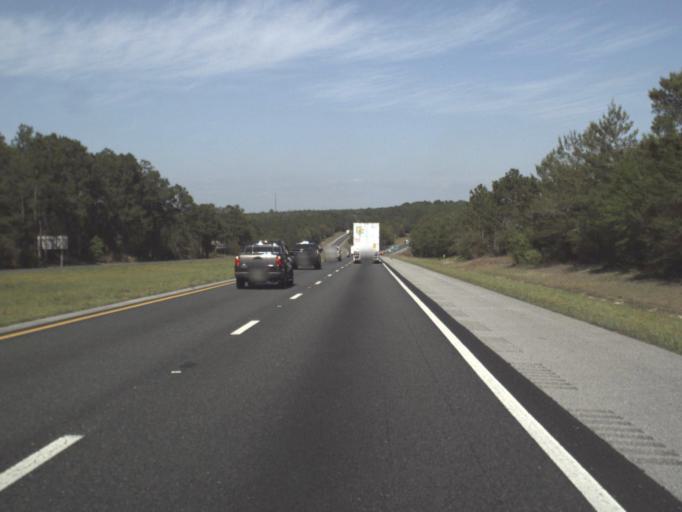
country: US
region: Florida
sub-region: Okaloosa County
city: Crestview
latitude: 30.7028
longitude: -86.7402
